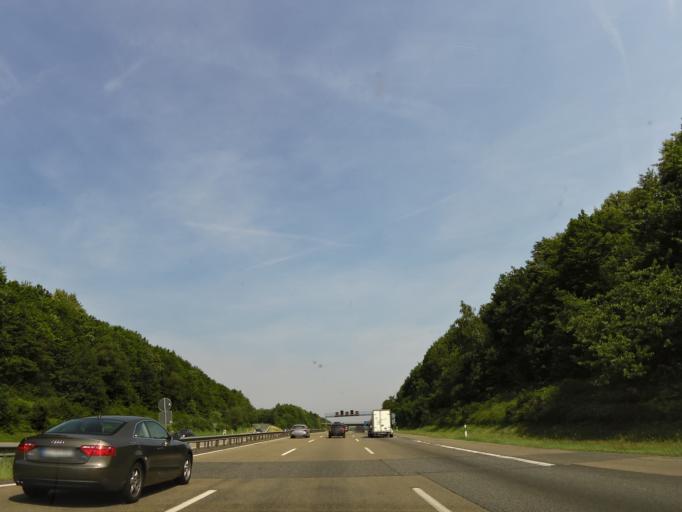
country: DE
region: Rheinland-Pfalz
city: Bell
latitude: 50.4048
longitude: 7.2384
